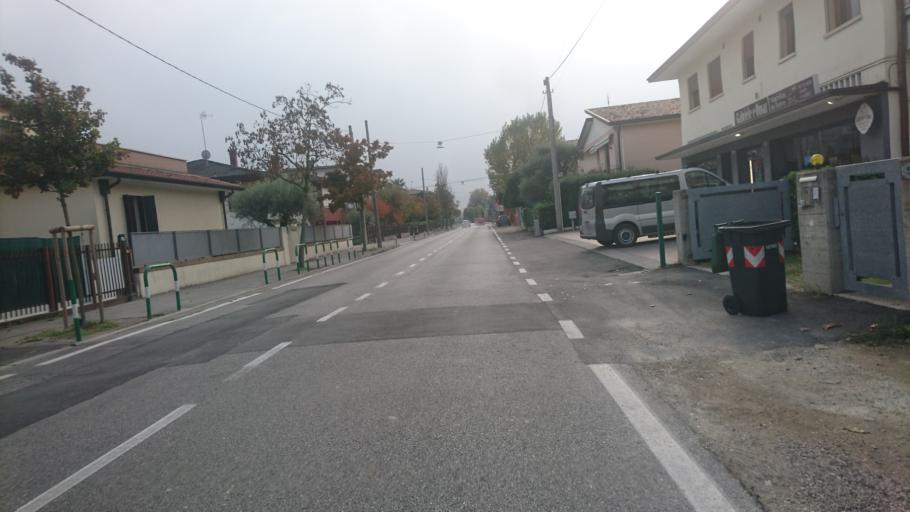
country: IT
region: Veneto
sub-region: Provincia di Padova
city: Cadoneghe
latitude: 45.4356
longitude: 11.9169
